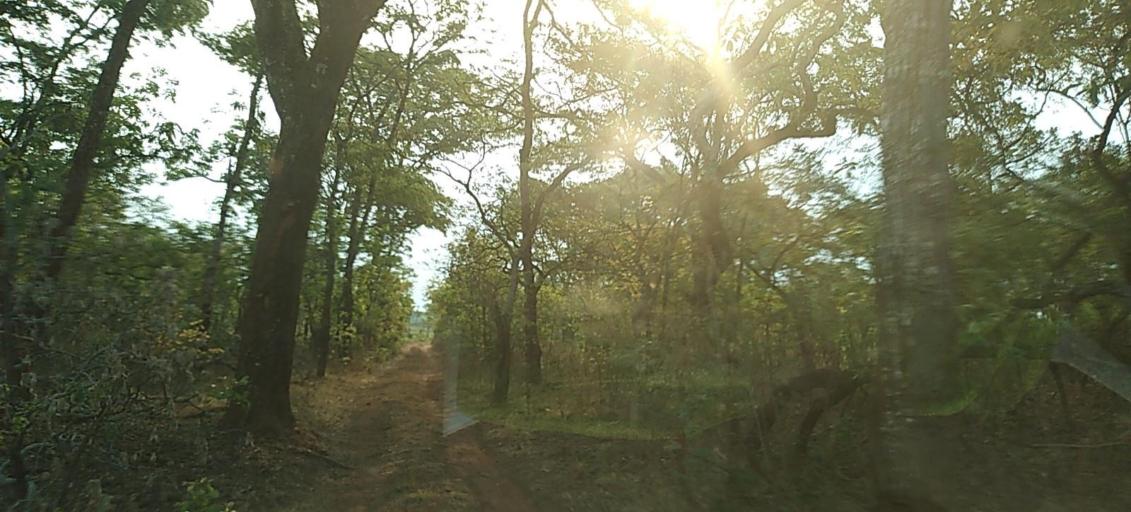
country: ZM
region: North-Western
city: Solwezi
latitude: -12.0418
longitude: 26.0350
